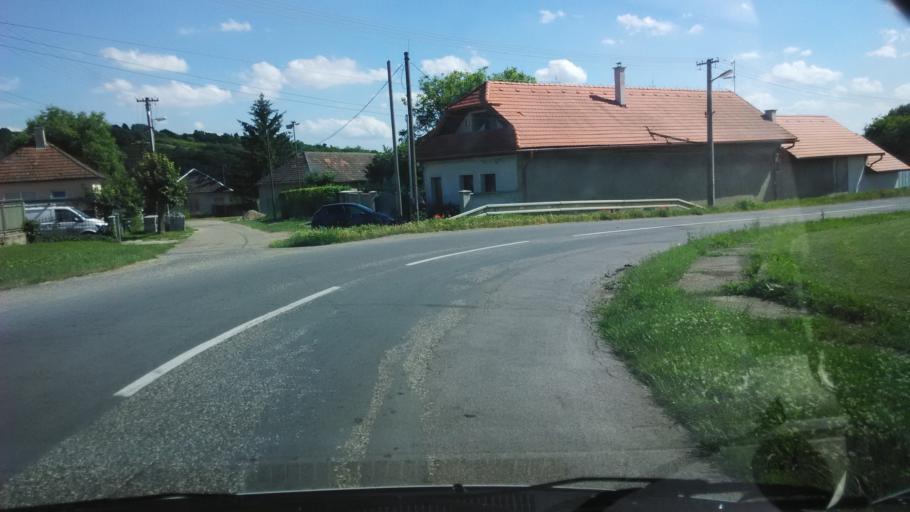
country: SK
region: Nitriansky
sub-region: Okres Nitra
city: Vrable
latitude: 48.1436
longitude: 18.4043
